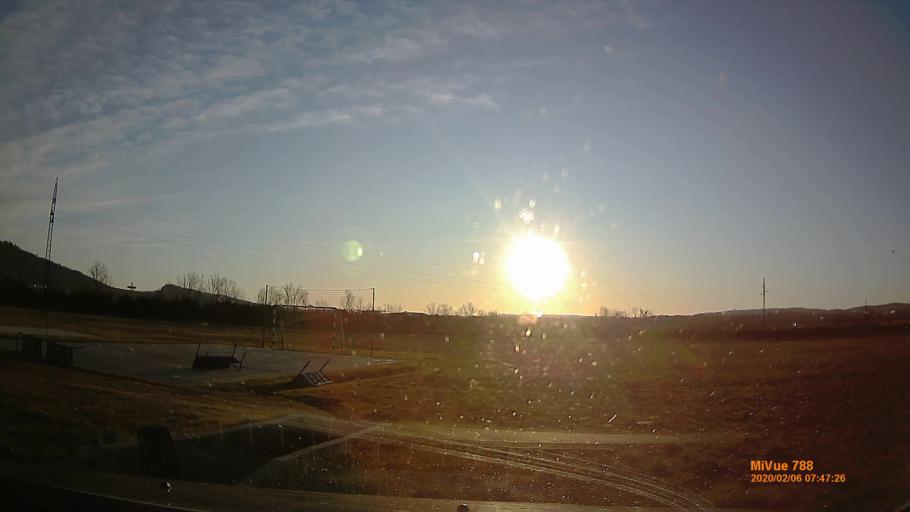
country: HU
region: Pest
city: Toeroekbalint
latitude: 47.4561
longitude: 18.8860
